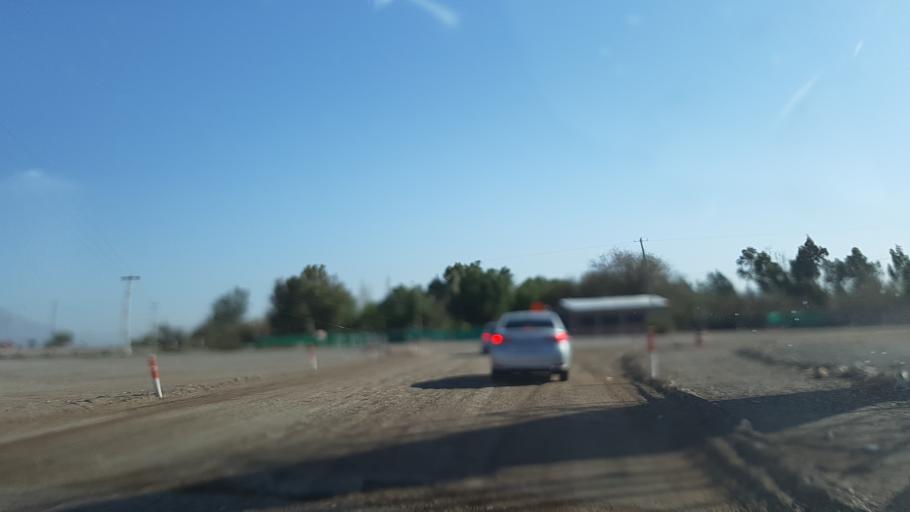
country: AR
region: San Juan
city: Villa Media Agua
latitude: -31.8738
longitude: -68.5272
